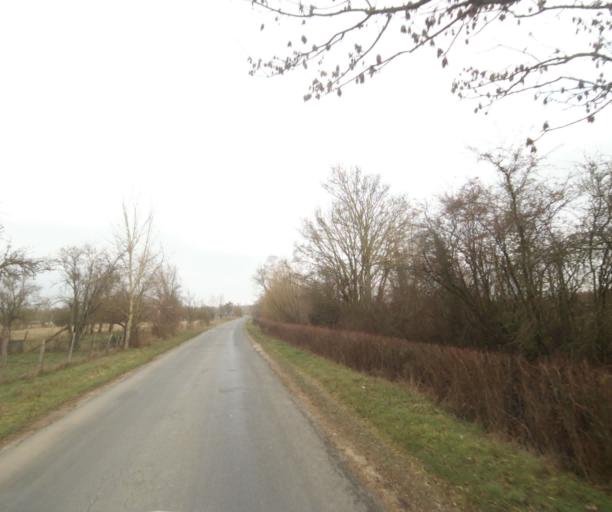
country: FR
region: Champagne-Ardenne
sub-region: Departement de la Haute-Marne
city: Villiers-en-Lieu
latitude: 48.6578
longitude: 4.8273
